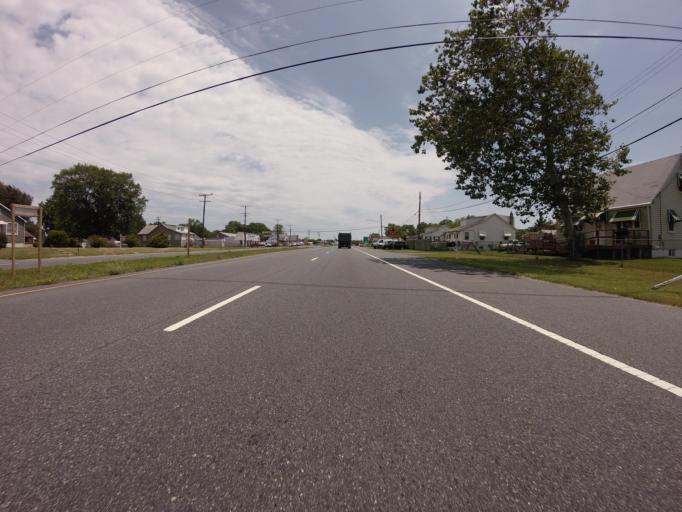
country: US
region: Maryland
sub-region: Baltimore County
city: Essex
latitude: 39.2770
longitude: -76.4781
